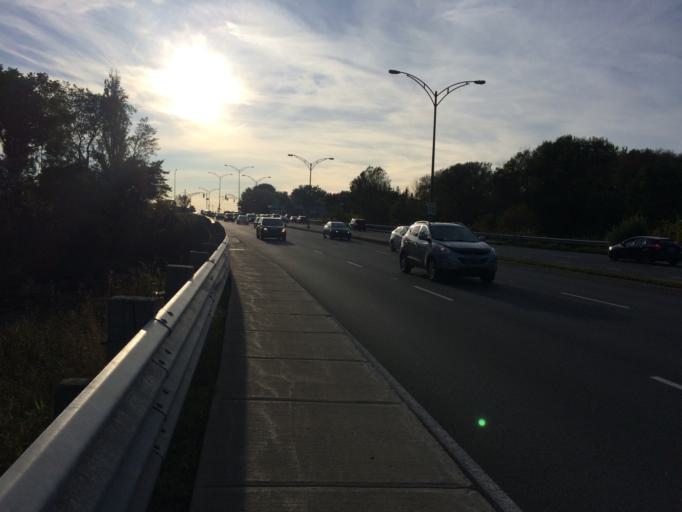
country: CA
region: Quebec
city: Quebec
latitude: 46.8082
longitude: -71.2672
